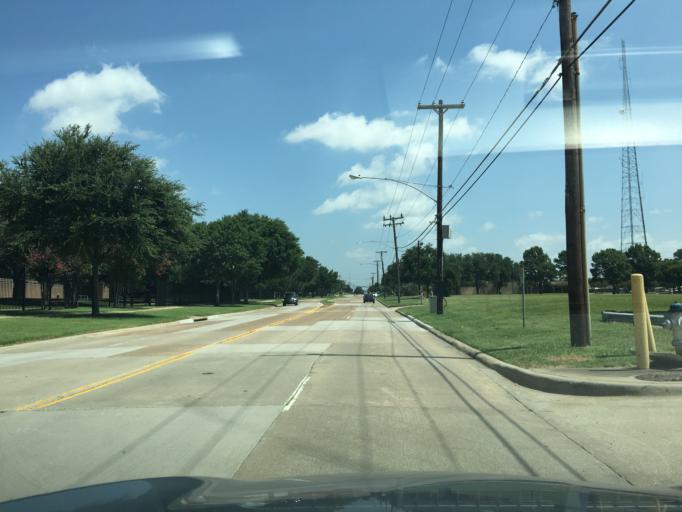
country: US
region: Texas
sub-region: Dallas County
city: Richardson
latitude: 32.9271
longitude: -96.7492
